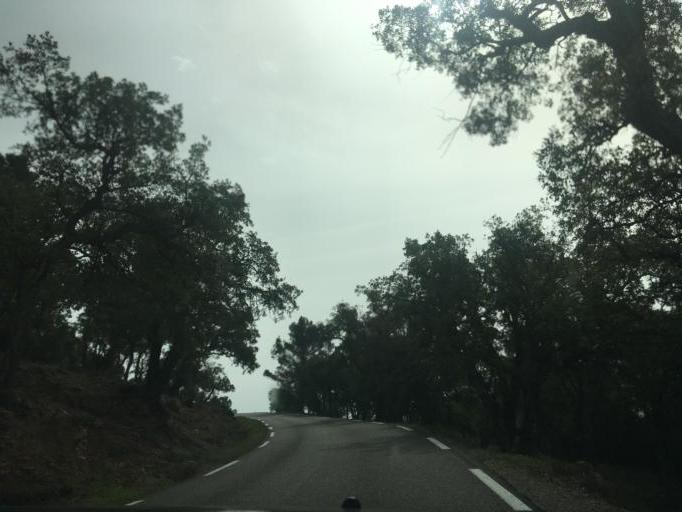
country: FR
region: Provence-Alpes-Cote d'Azur
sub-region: Departement du Var
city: Bagnols-en-Foret
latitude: 43.5158
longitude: 6.6442
